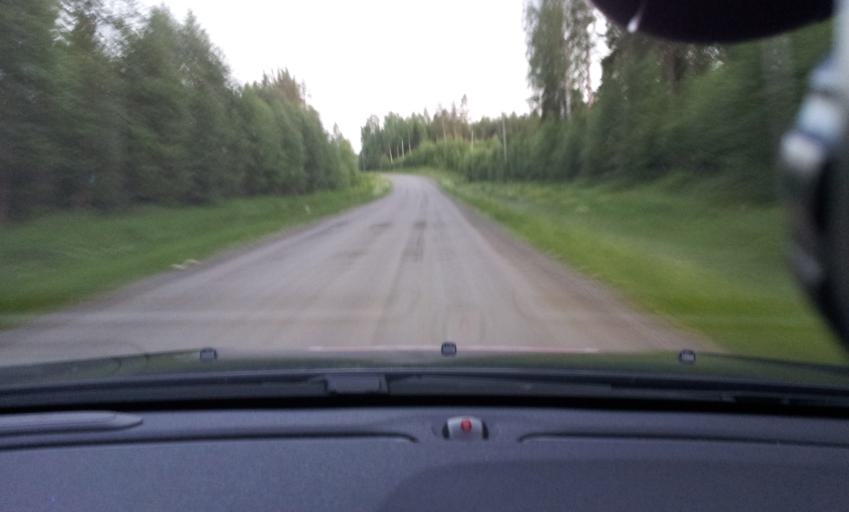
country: SE
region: Jaemtland
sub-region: Ragunda Kommun
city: Hammarstrand
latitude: 62.9312
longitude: 16.1293
